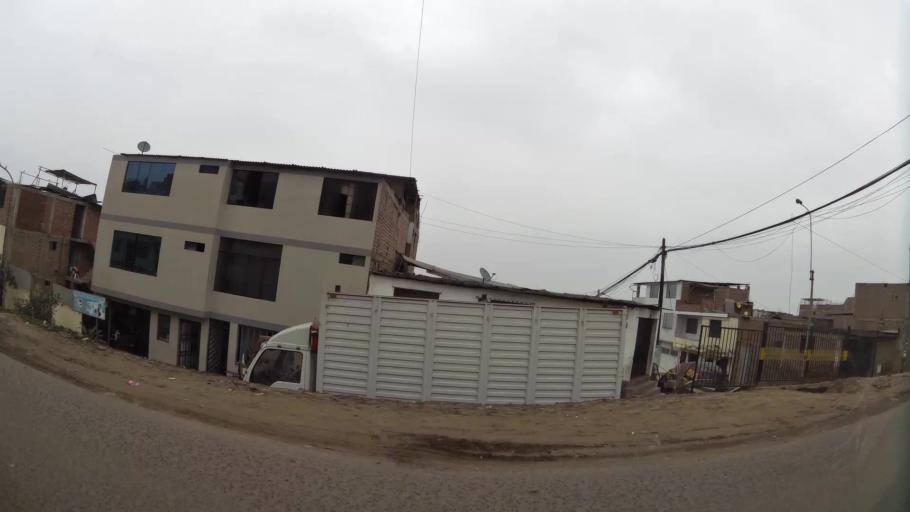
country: PE
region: Lima
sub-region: Lima
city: Surco
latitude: -12.1775
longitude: -76.9580
